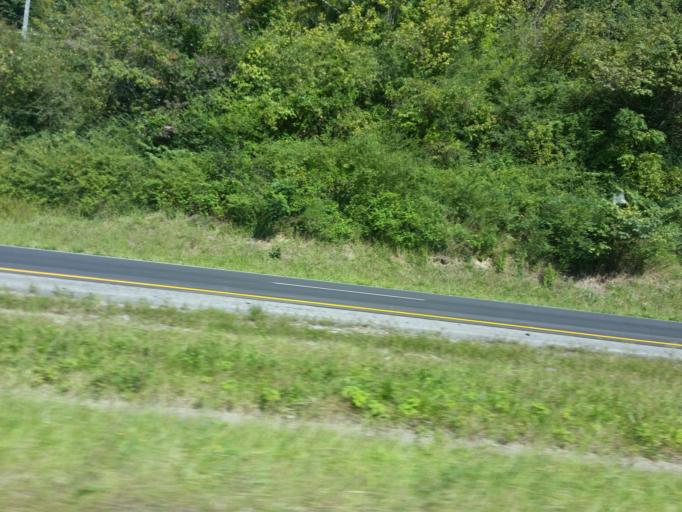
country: US
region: Kentucky
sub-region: Bell County
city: Pineville
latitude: 36.7332
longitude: -83.6945
